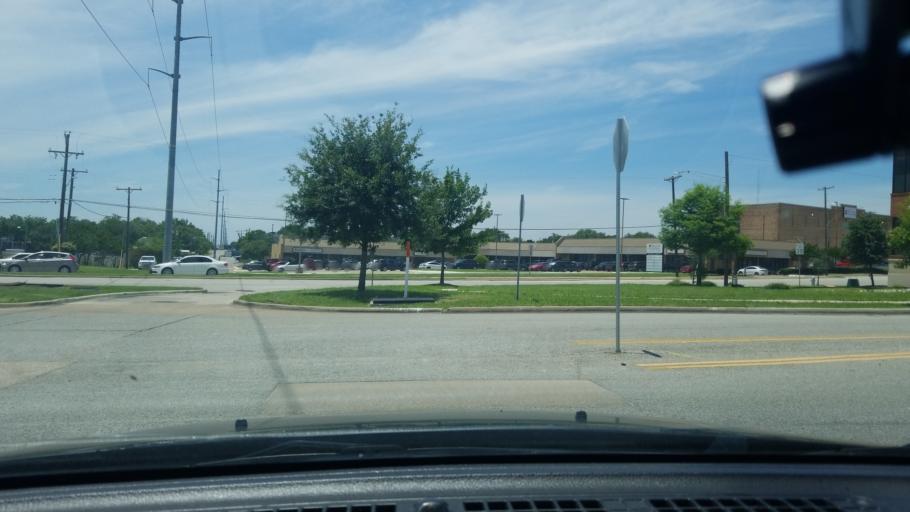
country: US
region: Texas
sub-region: Dallas County
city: Mesquite
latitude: 32.7758
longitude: -96.5987
